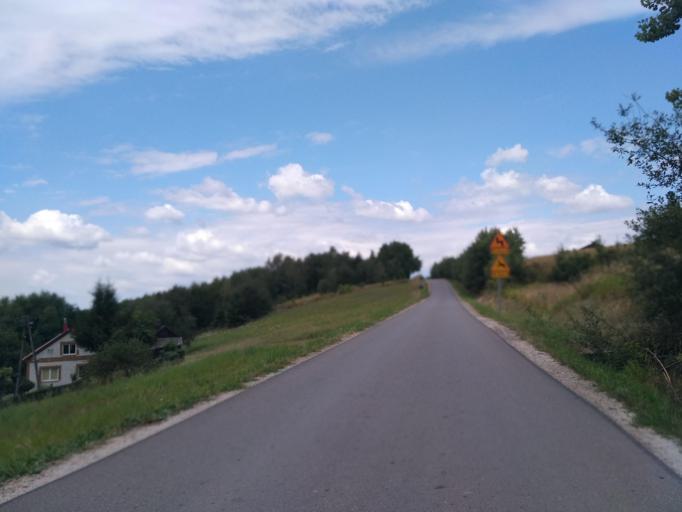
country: PL
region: Subcarpathian Voivodeship
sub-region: Powiat rzeszowski
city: Hyzne
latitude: 49.8993
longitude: 22.2300
